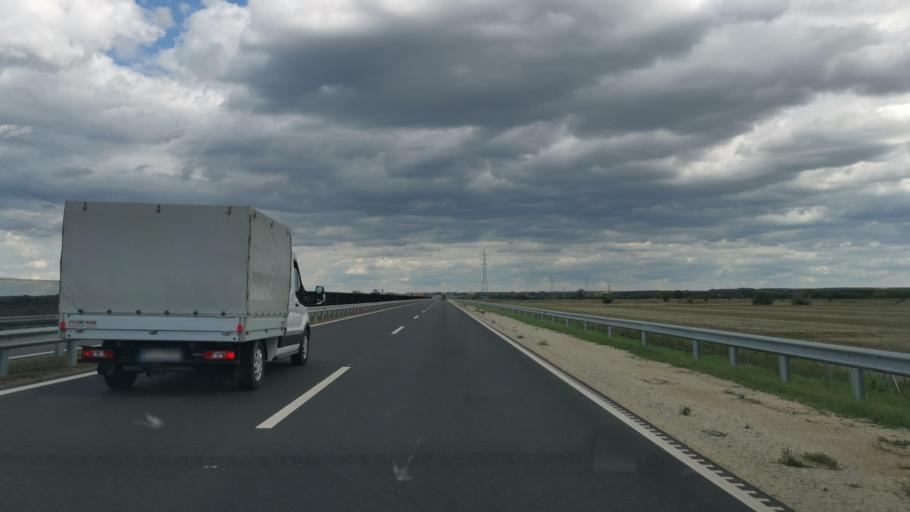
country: HU
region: Jasz-Nagykun-Szolnok
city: Szolnok
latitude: 47.2203
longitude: 20.2398
